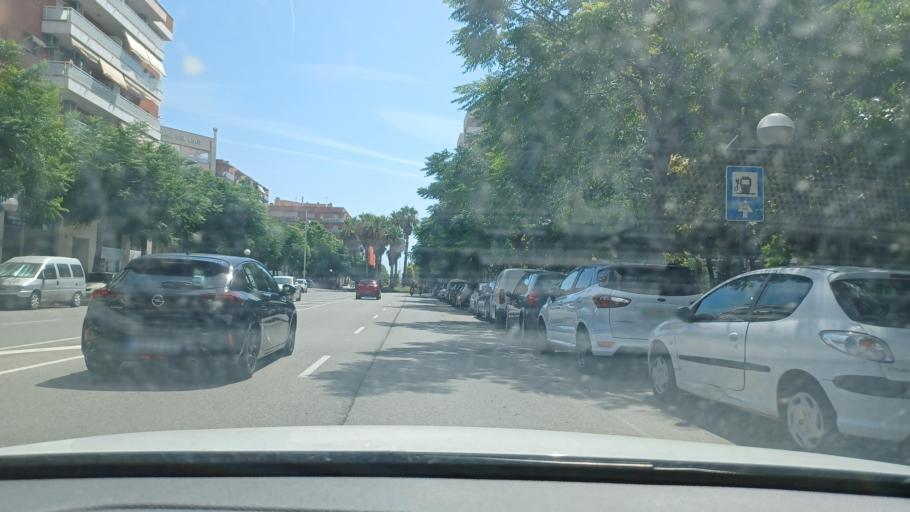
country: ES
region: Catalonia
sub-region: Provincia de Tarragona
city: Tarragona
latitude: 41.1146
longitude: 1.2408
